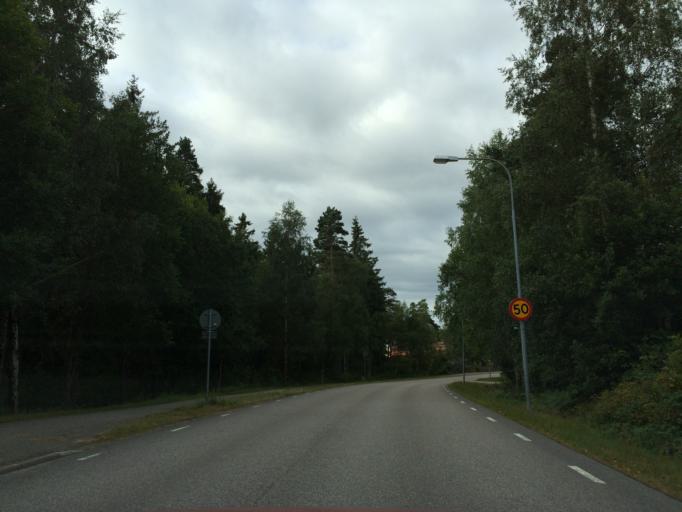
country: SE
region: Vaestra Goetaland
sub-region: Trollhattan
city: Trollhattan
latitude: 58.3200
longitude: 12.2774
